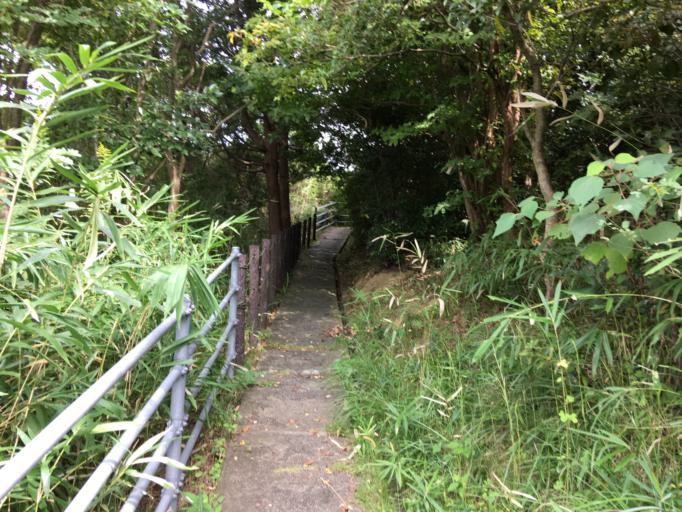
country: JP
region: Nara
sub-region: Ikoma-shi
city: Ikoma
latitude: 34.6179
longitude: 135.7022
